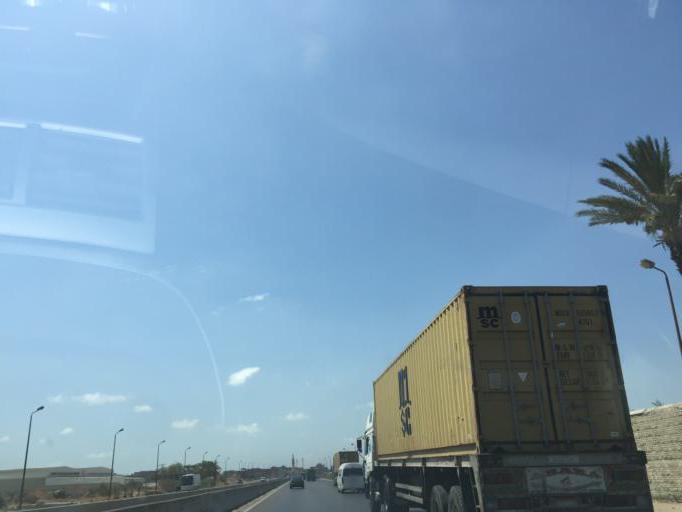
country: EG
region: Alexandria
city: Alexandria
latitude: 30.9749
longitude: 29.8211
